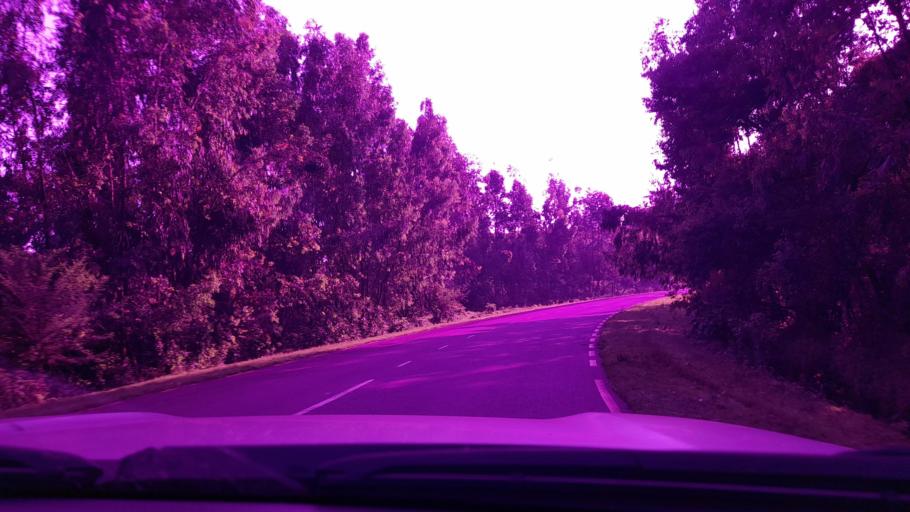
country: ET
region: Oromiya
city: Bedele
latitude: 8.1461
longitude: 36.4584
